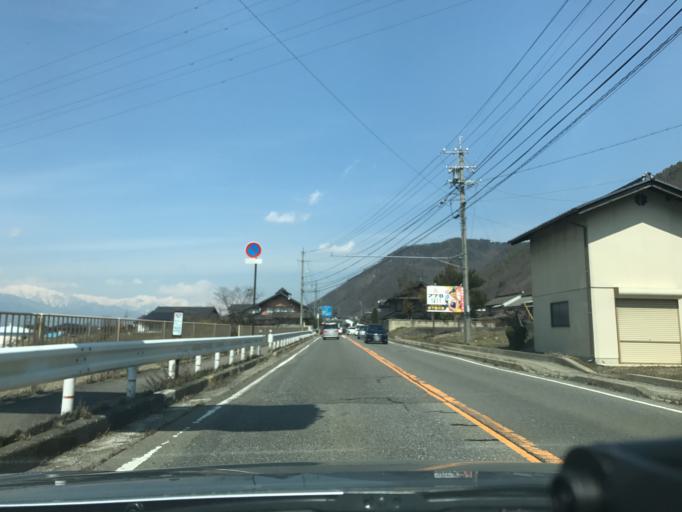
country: JP
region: Nagano
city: Toyoshina
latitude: 36.2989
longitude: 137.9408
